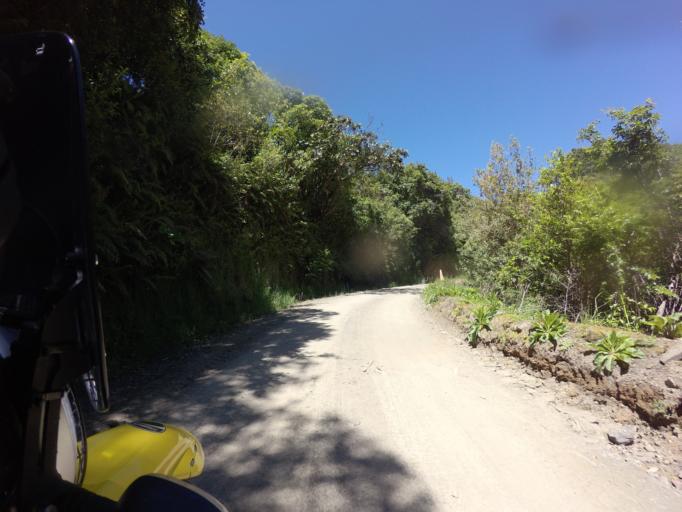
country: NZ
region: Bay of Plenty
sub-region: Opotiki District
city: Opotiki
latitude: -38.4086
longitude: 177.4197
